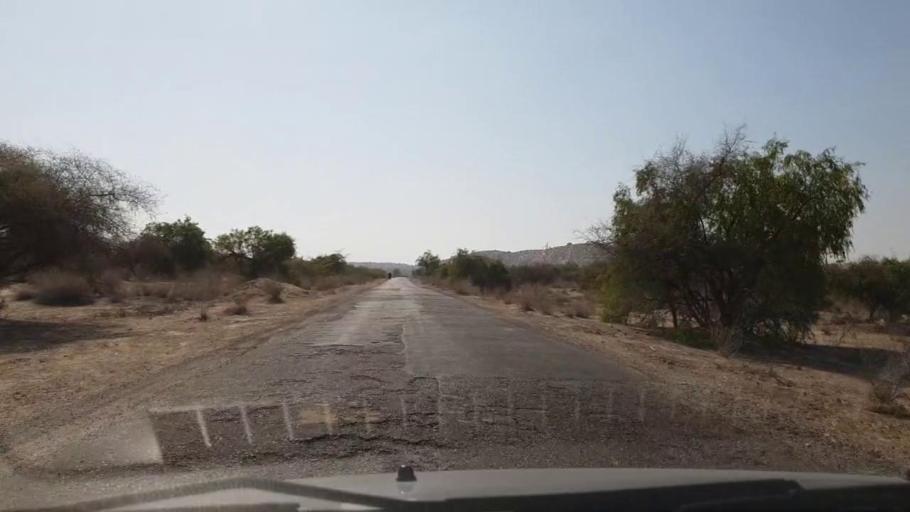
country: PK
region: Sindh
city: Mithi
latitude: 24.6498
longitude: 69.7505
